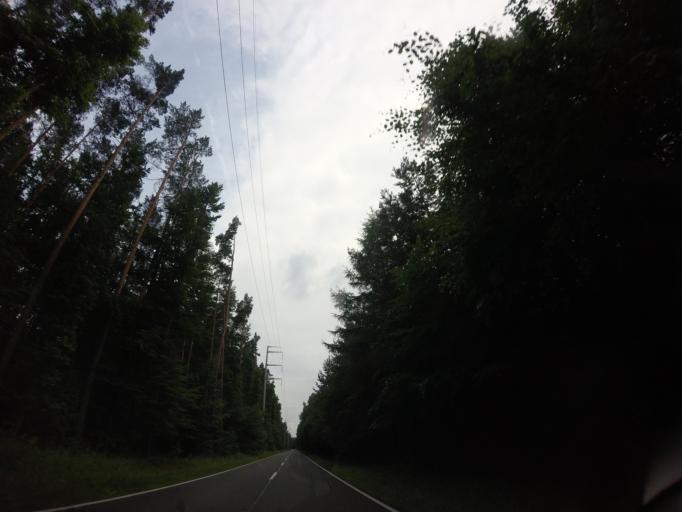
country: PL
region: West Pomeranian Voivodeship
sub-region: Powiat drawski
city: Wierzchowo
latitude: 53.4040
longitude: 16.1889
